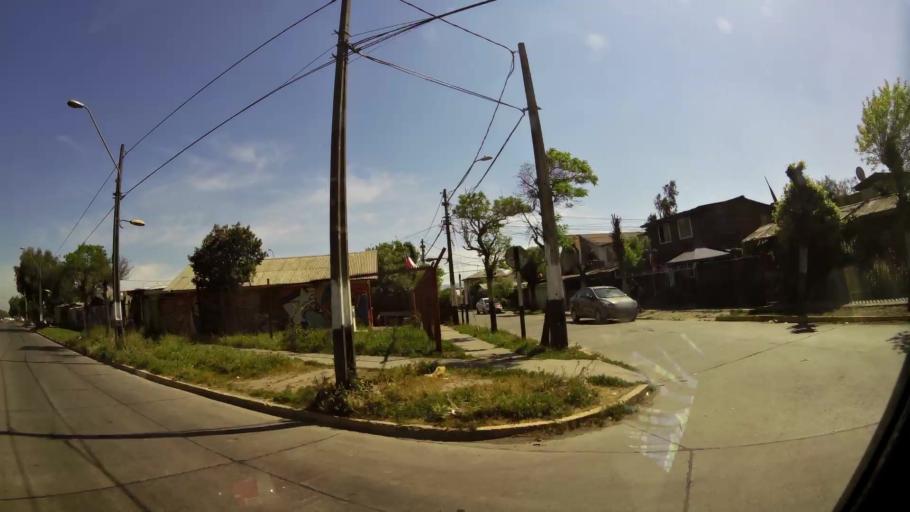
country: CL
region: Santiago Metropolitan
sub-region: Provincia de Santiago
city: Lo Prado
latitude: -33.5145
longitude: -70.7429
